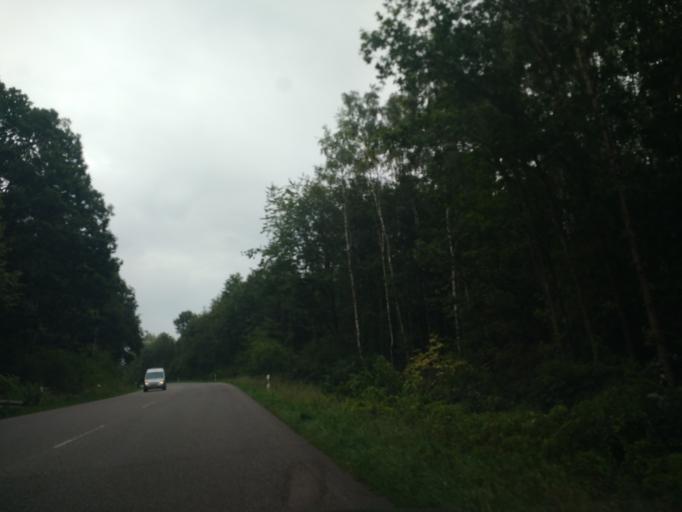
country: LU
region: Grevenmacher
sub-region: Canton de Remich
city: Remich
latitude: 49.5330
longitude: 6.4143
